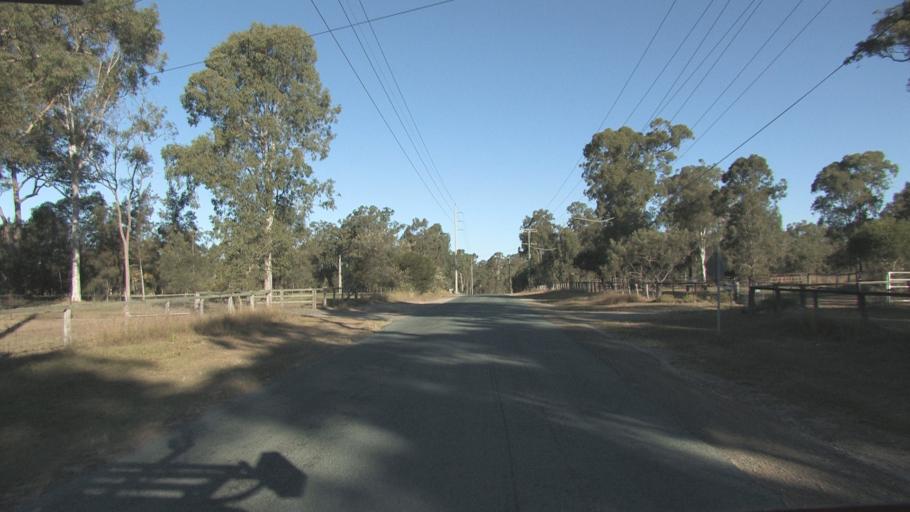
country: AU
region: Queensland
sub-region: Logan
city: North Maclean
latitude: -27.7913
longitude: 153.0419
